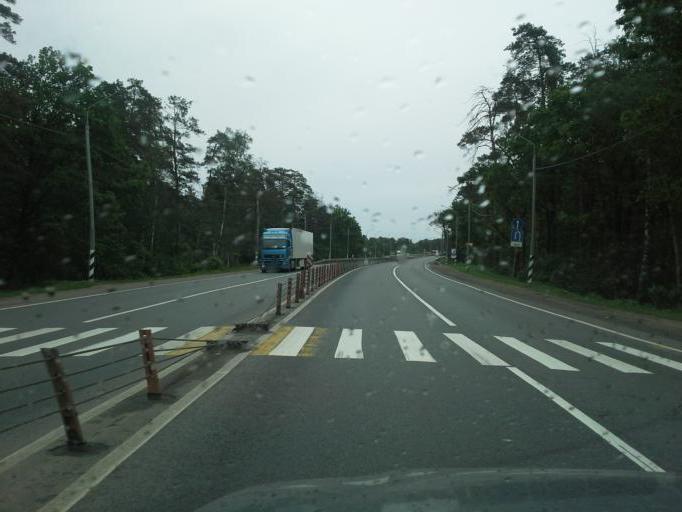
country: RU
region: Moskovskaya
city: Malaya Dubna
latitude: 55.8978
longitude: 39.0497
